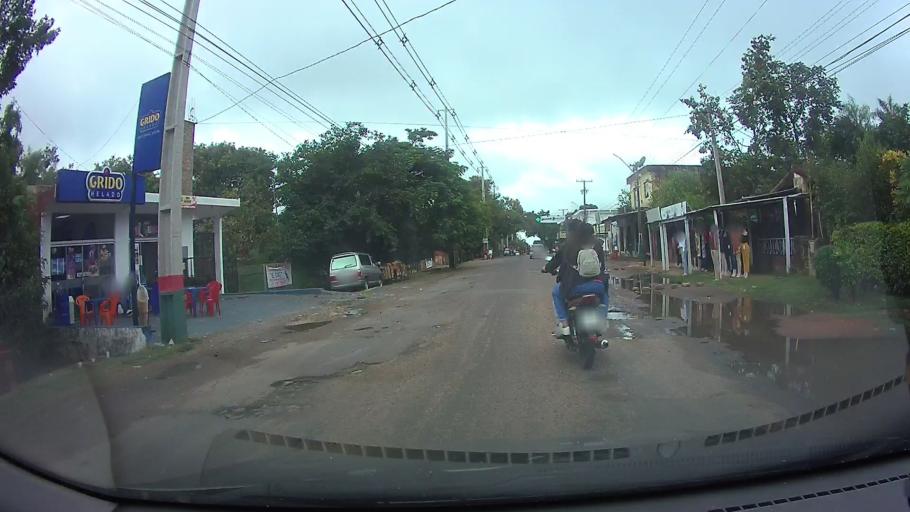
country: PY
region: Cordillera
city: Altos
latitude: -25.2665
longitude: -57.2509
